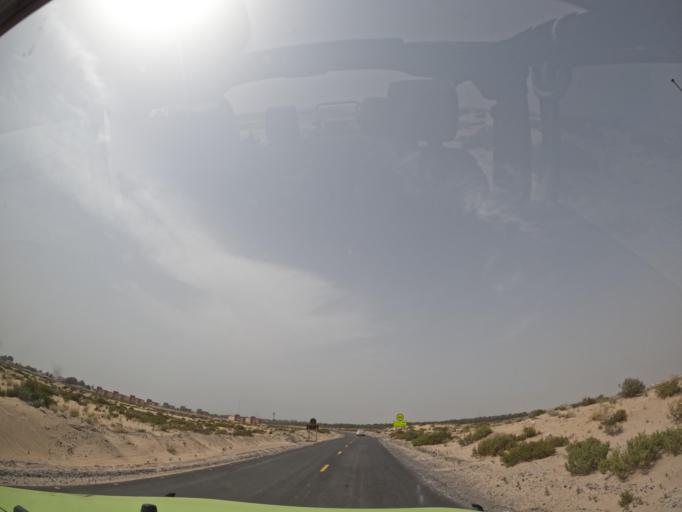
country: AE
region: Dubai
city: Dubai
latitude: 25.1290
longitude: 55.3414
